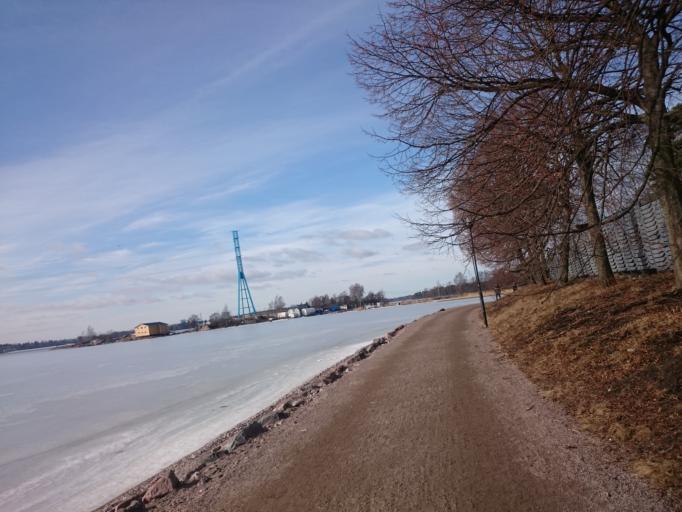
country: FI
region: Uusimaa
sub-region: Helsinki
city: Helsinki
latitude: 60.1705
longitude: 24.9068
